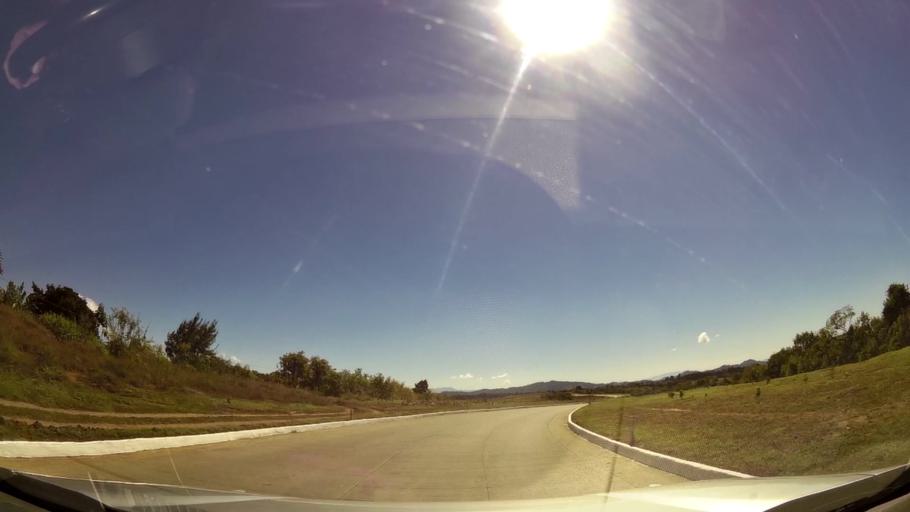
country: GT
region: Guatemala
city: San Jose Pinula
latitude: 14.5189
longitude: -90.4529
